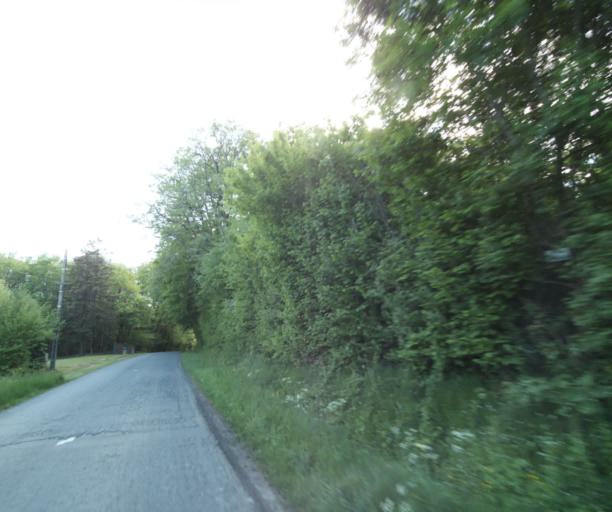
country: FR
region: Poitou-Charentes
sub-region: Departement de la Charente-Maritime
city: Chermignac
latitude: 45.7308
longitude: -0.6840
